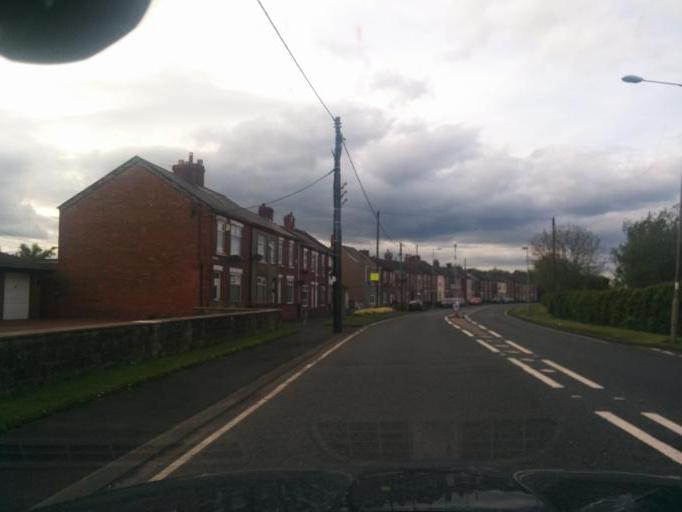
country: GB
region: England
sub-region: Northumberland
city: Ashington
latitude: 55.1533
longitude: -1.5767
